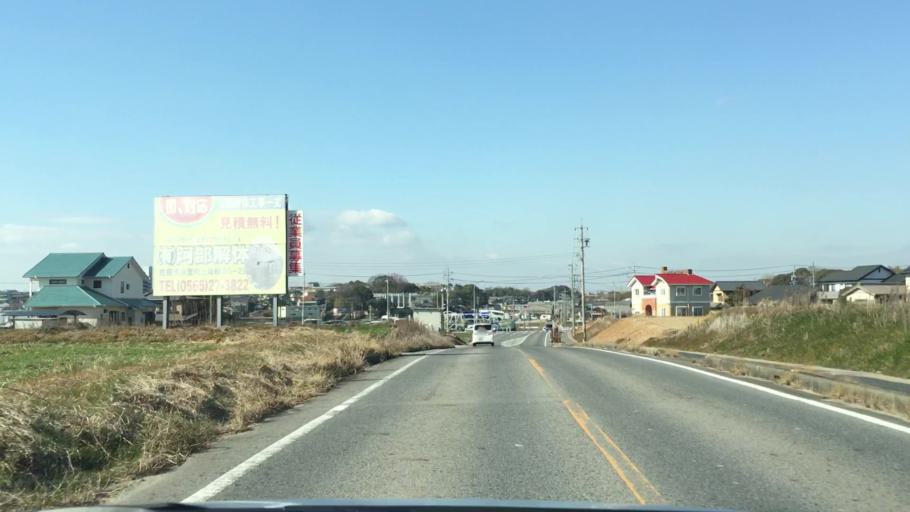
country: JP
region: Aichi
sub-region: Toyota-shi
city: Toyota
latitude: 35.0417
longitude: 137.1198
